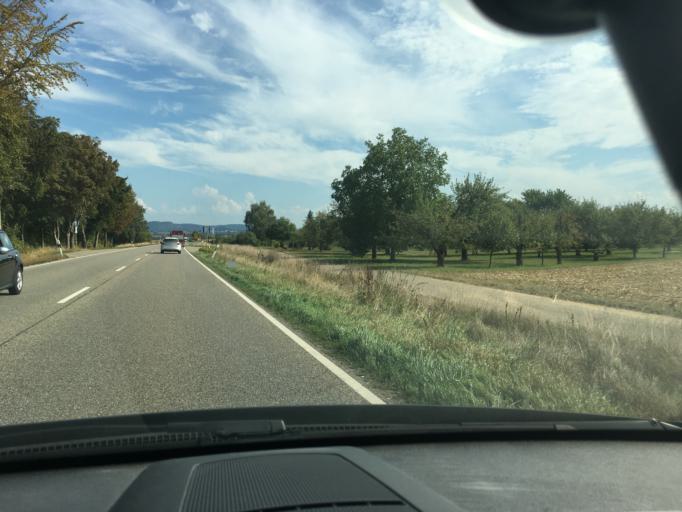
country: DE
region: Baden-Wuerttemberg
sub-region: Regierungsbezirk Stuttgart
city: Stuttgart Muehlhausen
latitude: 48.8857
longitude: 9.2462
